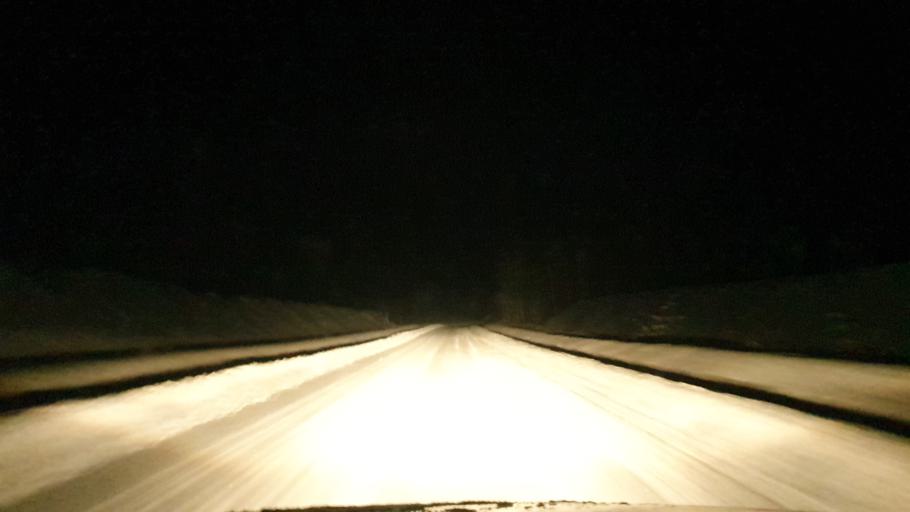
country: EE
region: Vorumaa
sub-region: Antsla vald
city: Vana-Antsla
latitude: 57.9686
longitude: 26.7479
